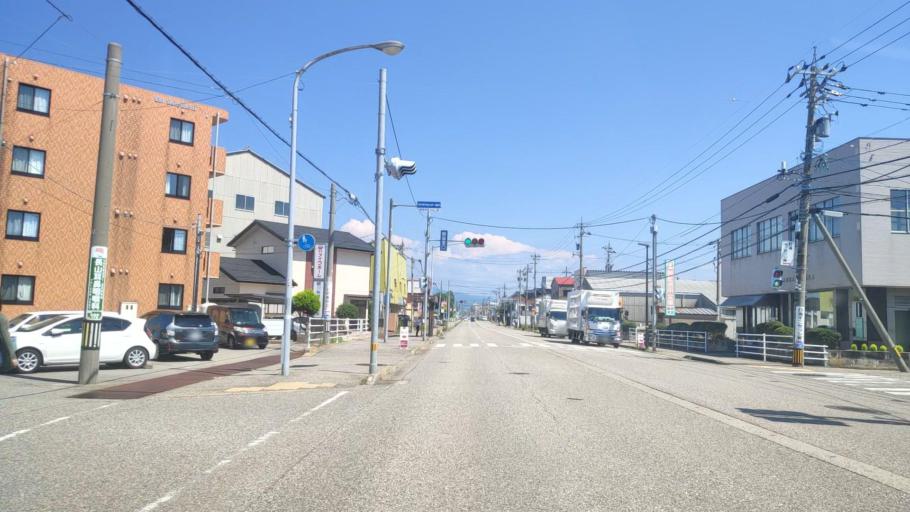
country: JP
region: Ishikawa
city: Kanazawa-shi
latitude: 36.5938
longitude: 136.6078
